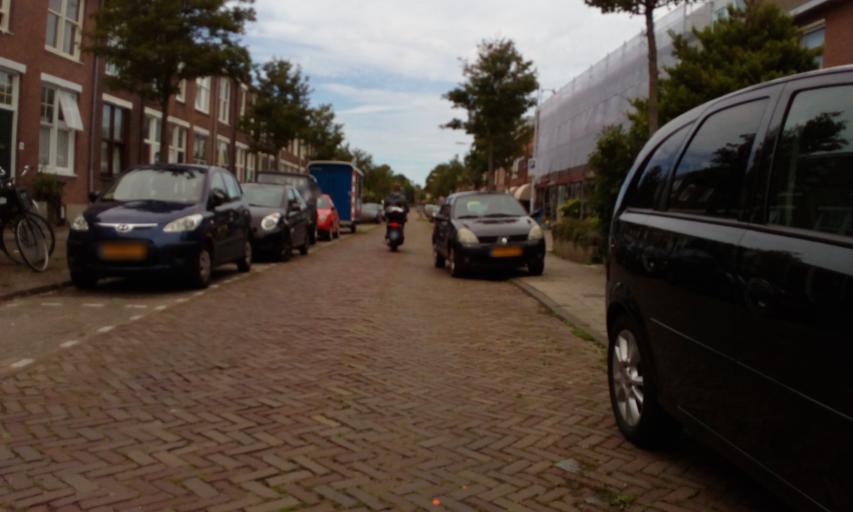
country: NL
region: South Holland
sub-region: Gemeente Leidschendam-Voorburg
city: Voorburg
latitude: 52.0747
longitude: 4.3879
